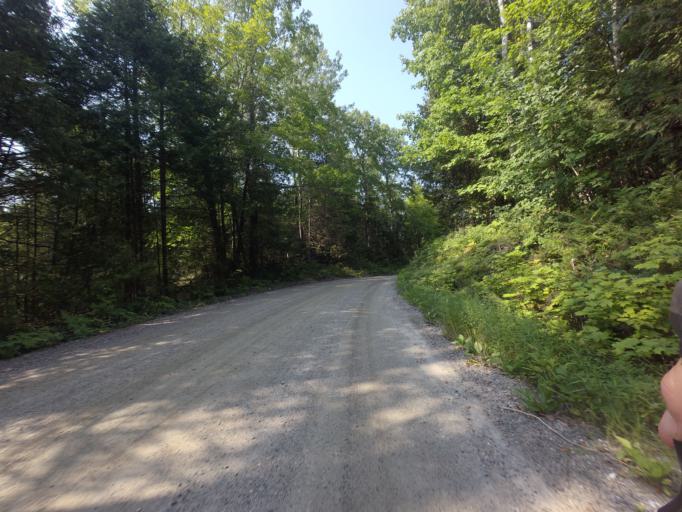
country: CA
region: Ontario
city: Skatepark
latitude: 44.7590
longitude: -76.8241
